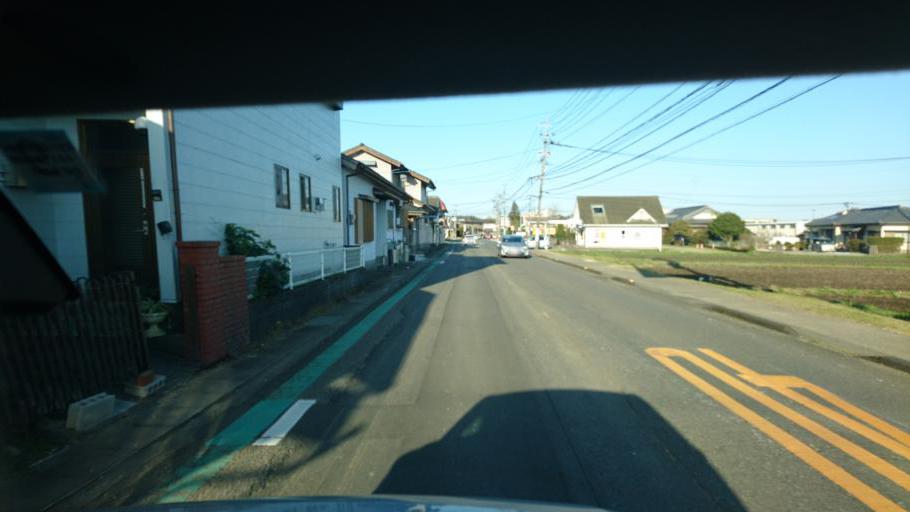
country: JP
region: Miyazaki
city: Miyazaki-shi
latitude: 31.8458
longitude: 131.3954
